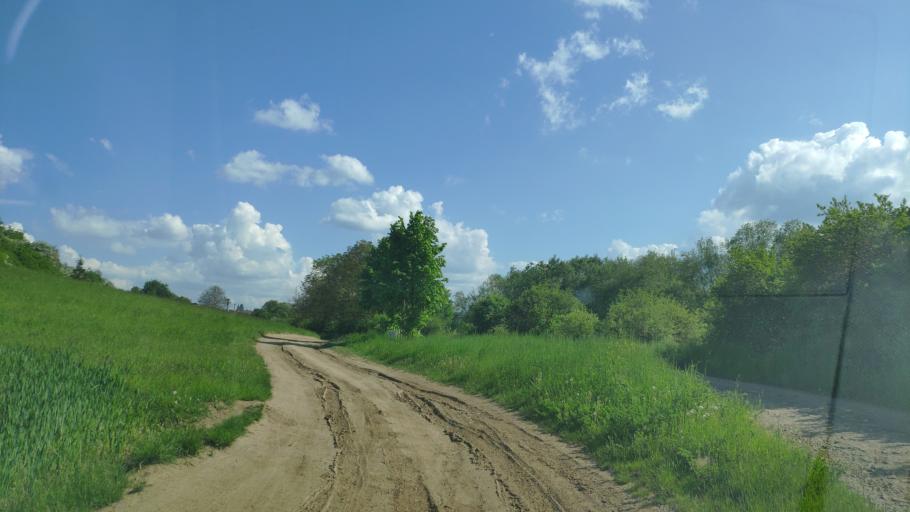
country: SK
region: Presovsky
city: Sabinov
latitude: 49.0520
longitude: 21.1437
